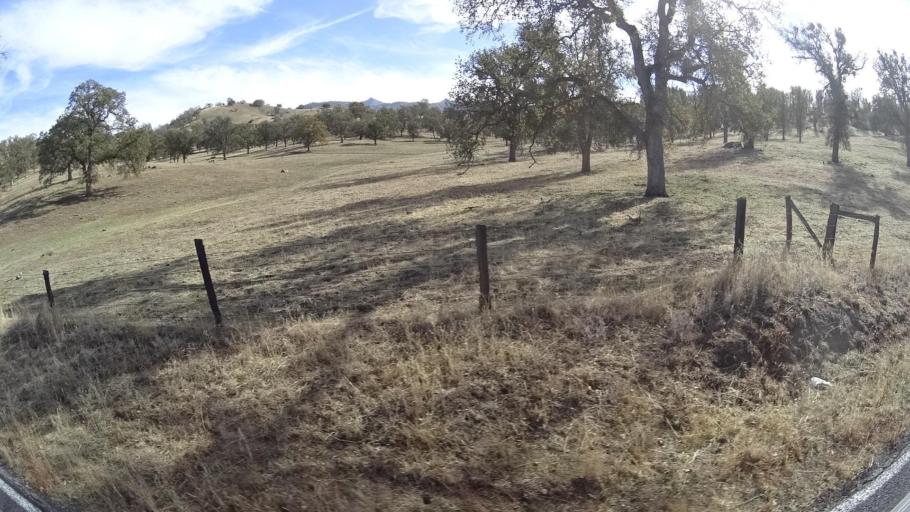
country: US
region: California
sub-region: Kern County
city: Alta Sierra
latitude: 35.6800
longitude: -118.7333
